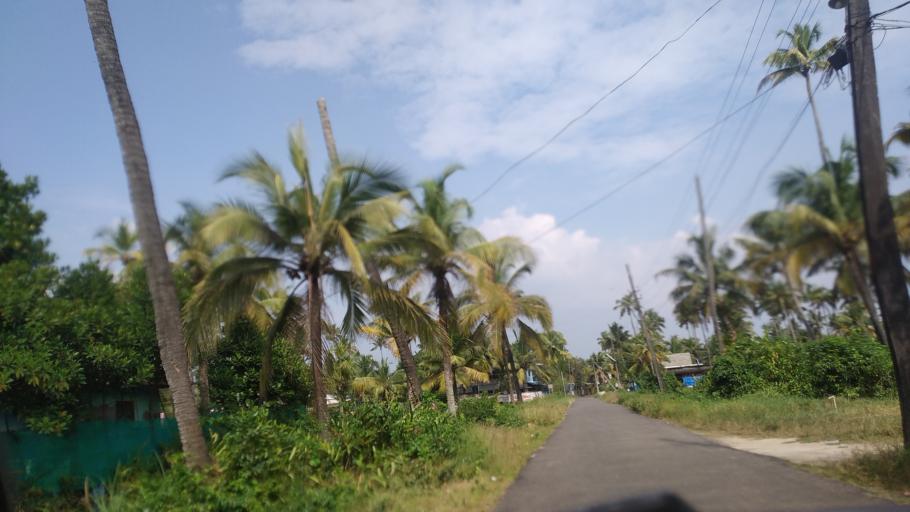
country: IN
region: Kerala
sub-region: Ernakulam
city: Elur
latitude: 10.0870
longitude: 76.1995
